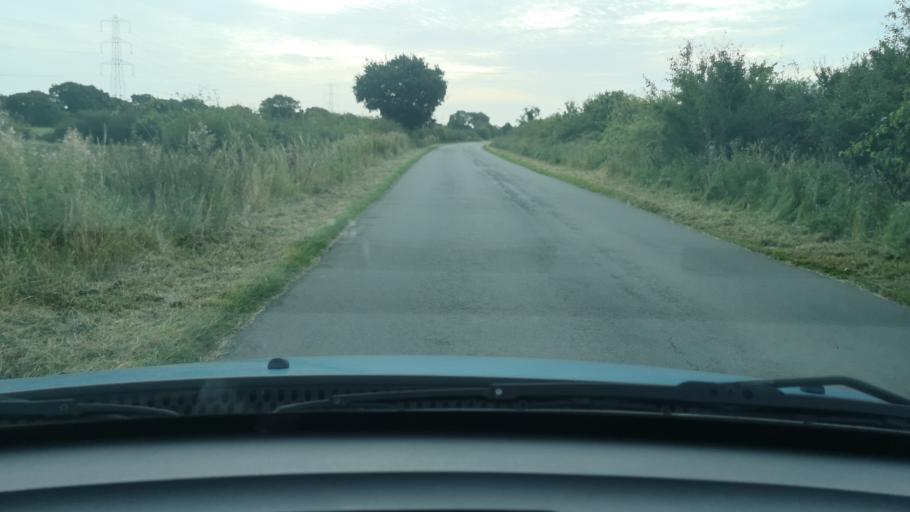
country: GB
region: England
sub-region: Doncaster
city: Stainforth
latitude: 53.6299
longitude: -1.0277
